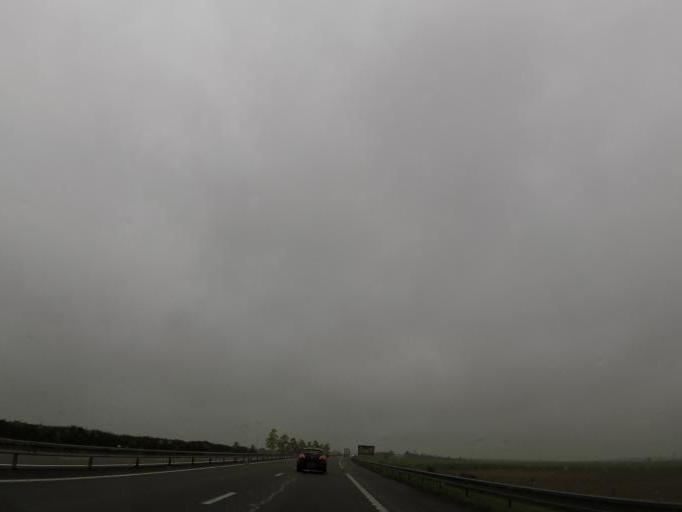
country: FR
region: Champagne-Ardenne
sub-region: Departement de la Marne
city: Saint-Memmie
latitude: 49.0338
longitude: 4.4016
